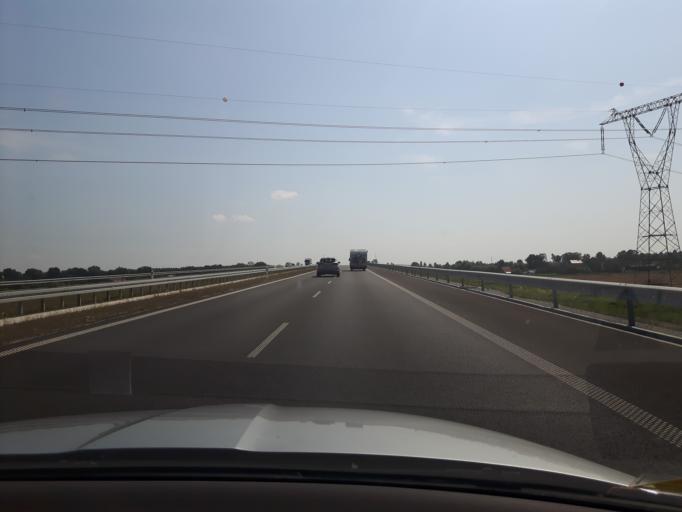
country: PL
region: Warmian-Masurian Voivodeship
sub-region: Powiat elblaski
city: Gronowo Elblaskie
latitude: 54.1678
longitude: 19.2320
